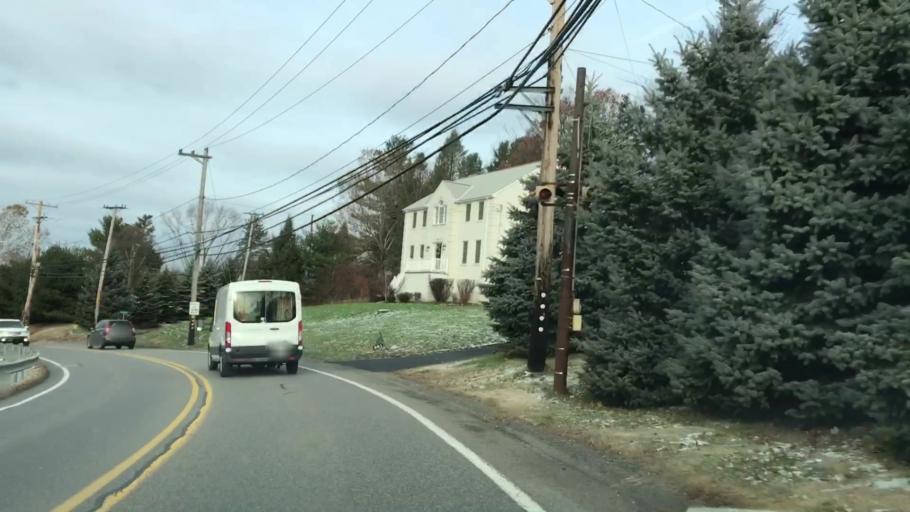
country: US
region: Pennsylvania
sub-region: Allegheny County
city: Carnegie
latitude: 40.4040
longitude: -80.0702
